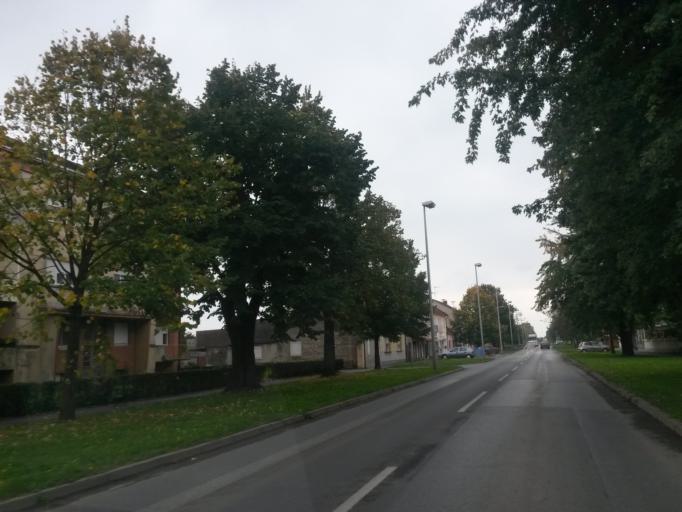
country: HR
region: Osjecko-Baranjska
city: Piskorevci
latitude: 45.3107
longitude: 18.4160
